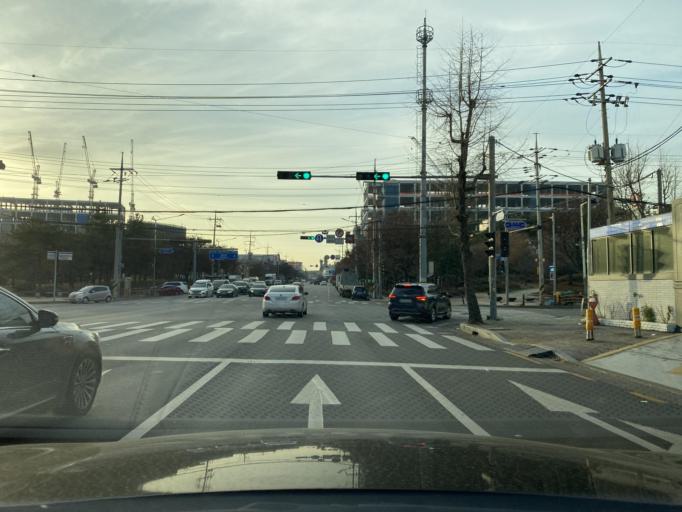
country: KR
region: Incheon
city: Incheon
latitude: 37.5066
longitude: 126.6687
